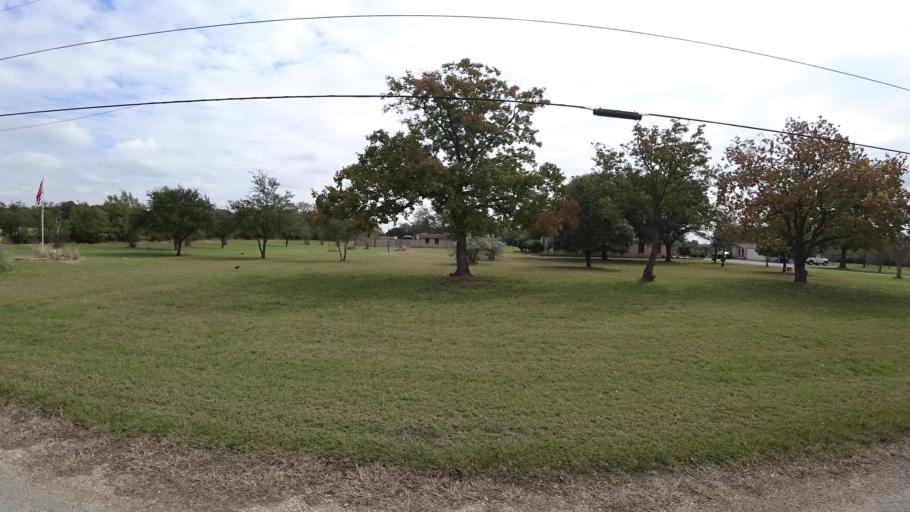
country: US
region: Texas
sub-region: Travis County
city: Shady Hollow
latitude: 30.2079
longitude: -97.8988
